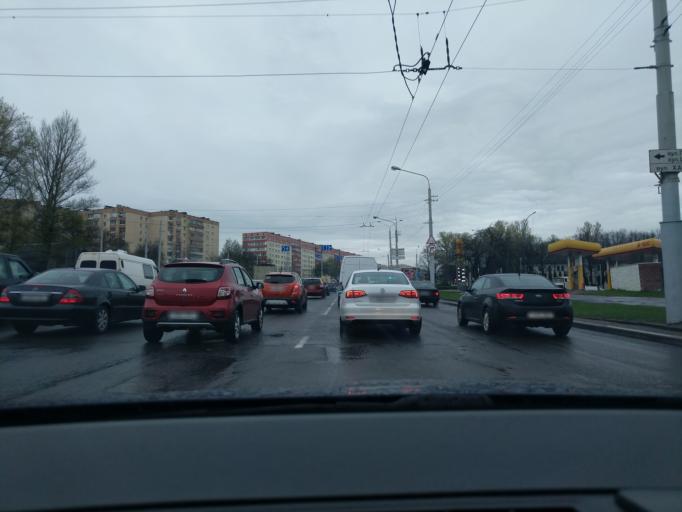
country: BY
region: Minsk
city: Novoye Medvezhino
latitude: 53.8938
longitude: 27.4988
